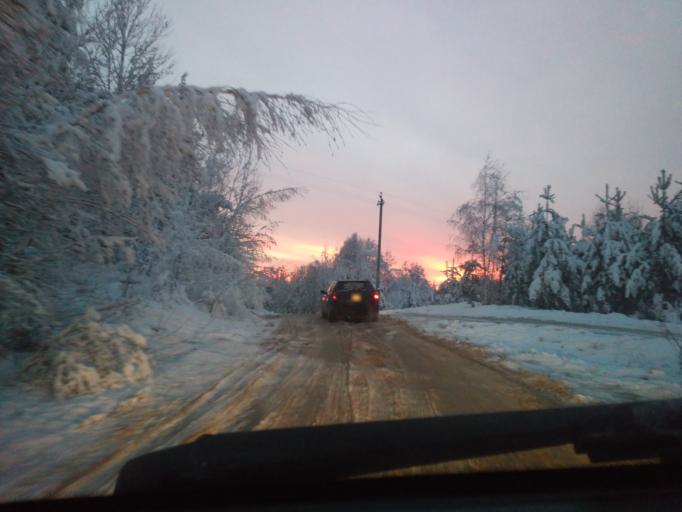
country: BY
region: Minsk
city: Horad Barysaw
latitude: 54.2573
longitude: 28.4113
